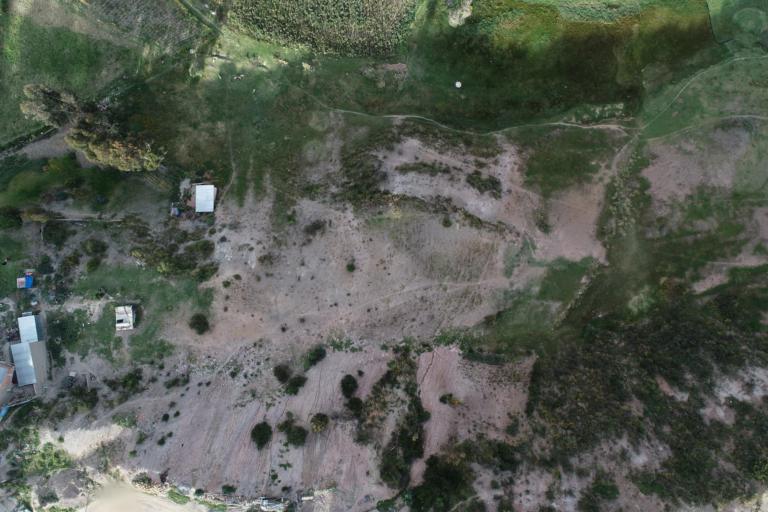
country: BO
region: La Paz
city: La Paz
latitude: -16.5436
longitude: -68.0026
